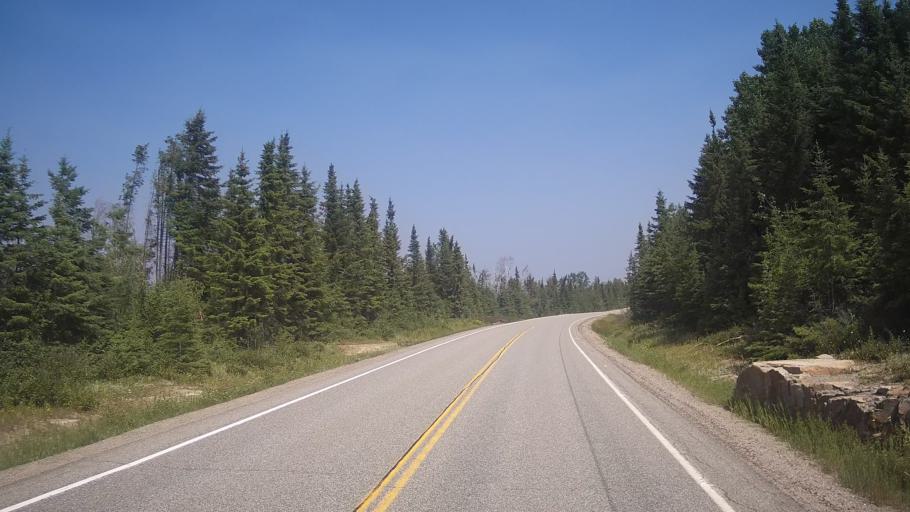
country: CA
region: Ontario
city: Timmins
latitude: 48.0448
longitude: -81.5838
